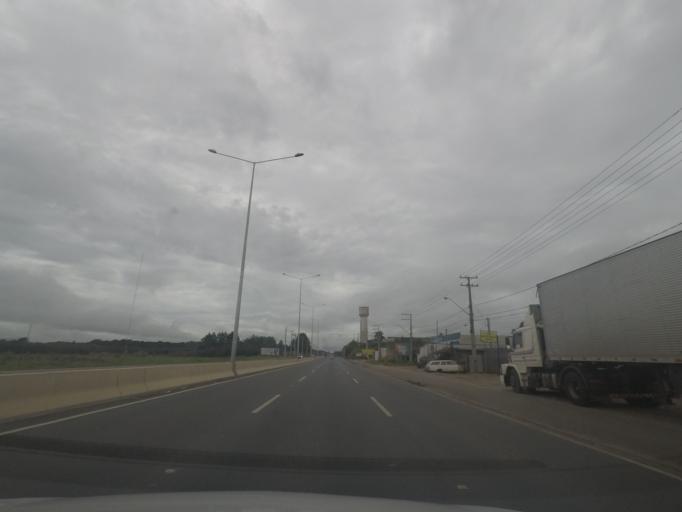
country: BR
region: Parana
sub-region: Piraquara
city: Piraquara
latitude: -25.4493
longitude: -49.1284
